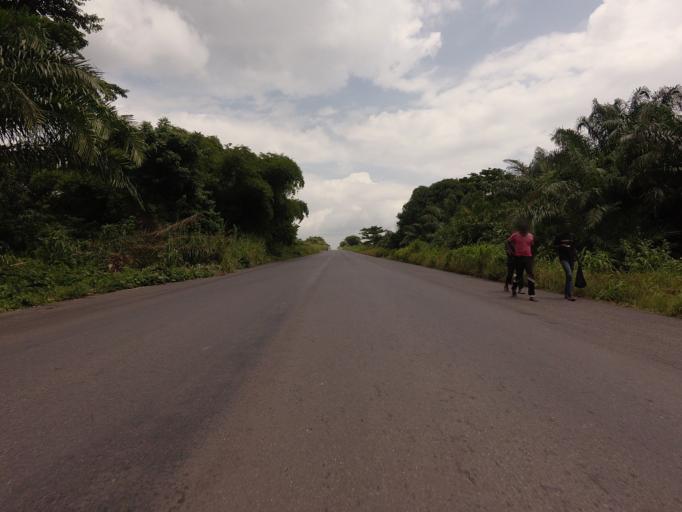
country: GH
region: Volta
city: Ho
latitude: 6.5595
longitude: 0.2629
